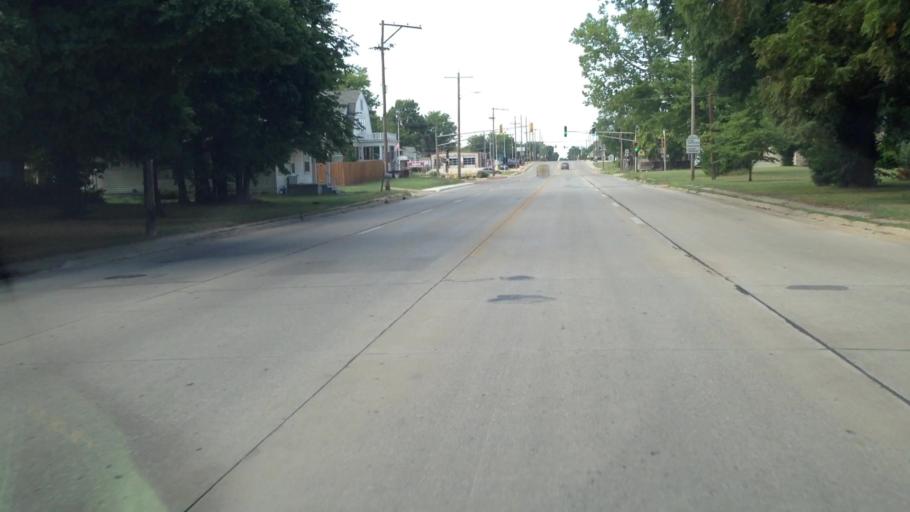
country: US
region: Kansas
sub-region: Labette County
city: Parsons
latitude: 37.3367
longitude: -95.2592
